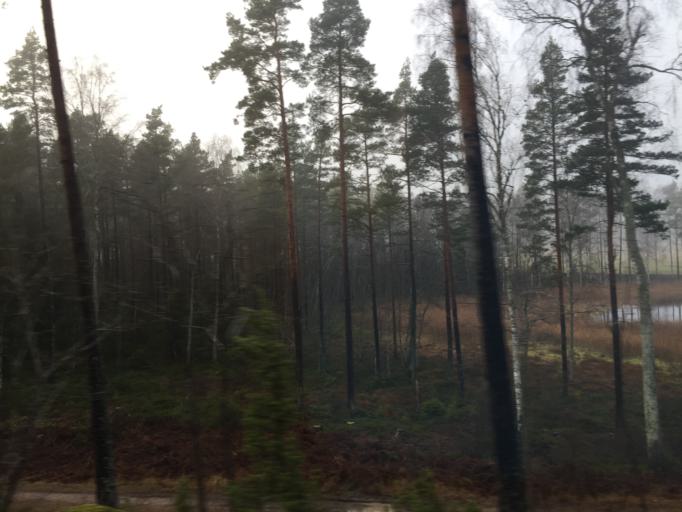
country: SE
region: Stockholm
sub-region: Nynashamns Kommun
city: Osmo
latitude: 59.0684
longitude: 17.8759
